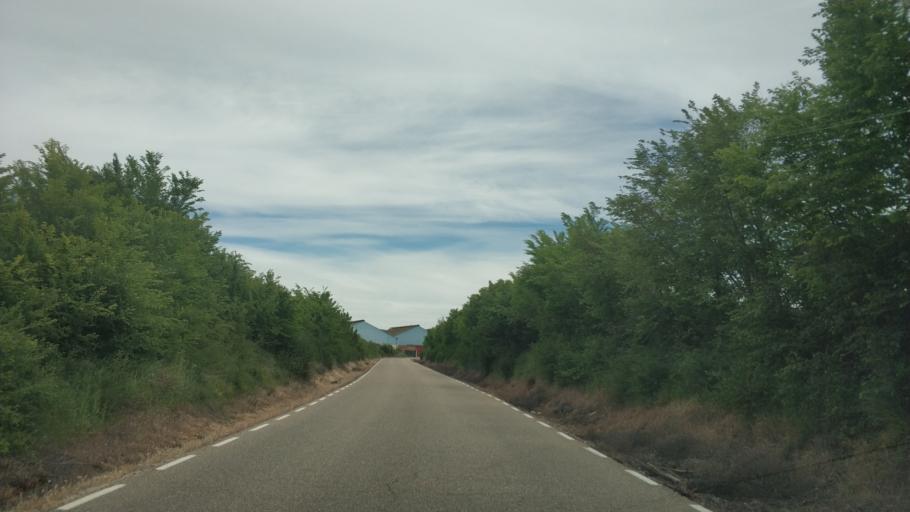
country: ES
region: Castille and Leon
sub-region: Provincia de Soria
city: Berlanga de Duero
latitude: 41.4813
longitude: -2.8644
